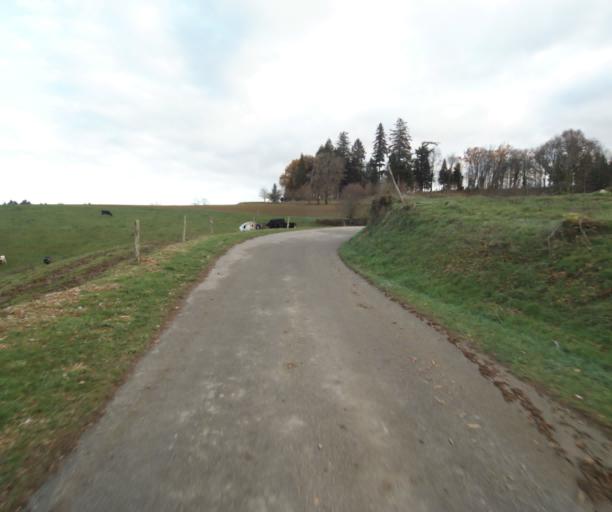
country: FR
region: Limousin
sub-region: Departement de la Correze
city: Laguenne
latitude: 45.2281
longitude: 1.7749
